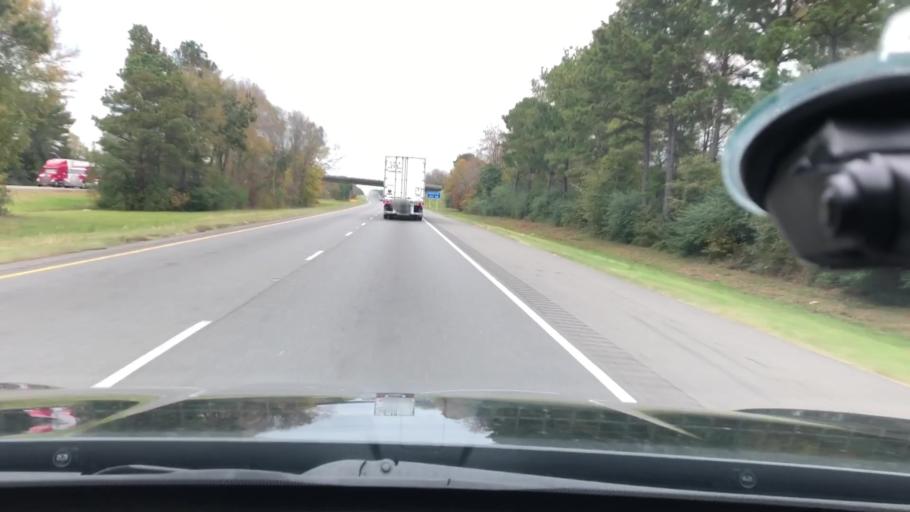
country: US
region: Arkansas
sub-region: Hempstead County
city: Hope
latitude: 33.6676
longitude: -93.6300
